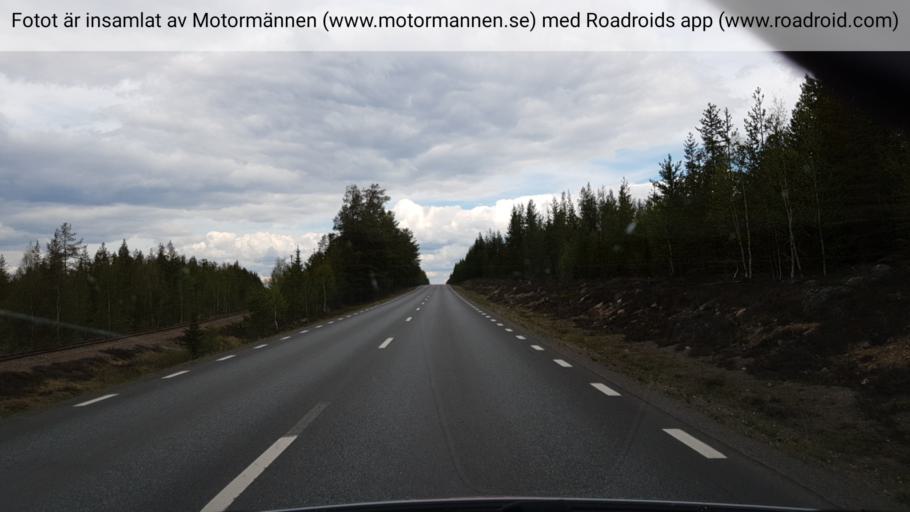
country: SE
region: Norrbotten
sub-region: Arvidsjaurs Kommun
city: Arvidsjaur
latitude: 65.5375
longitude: 19.2376
